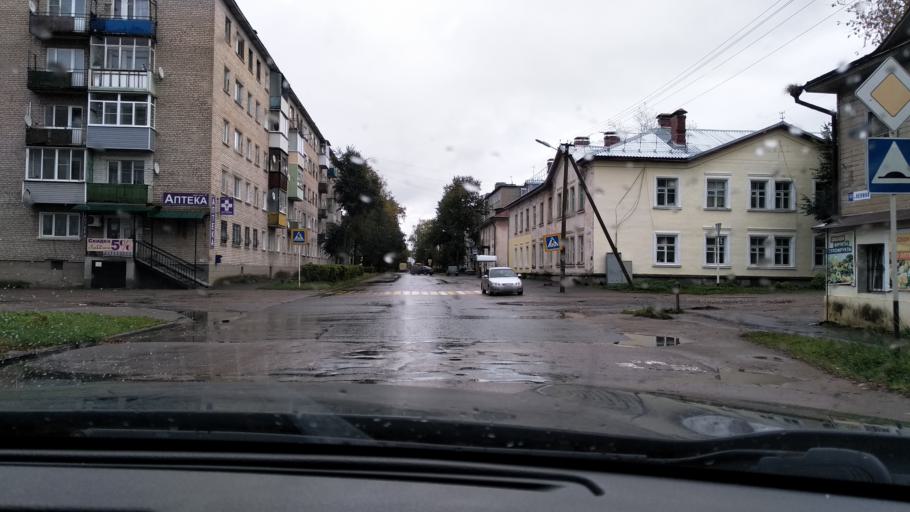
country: RU
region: Tverskaya
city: Kashin
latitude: 57.3561
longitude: 37.5995
